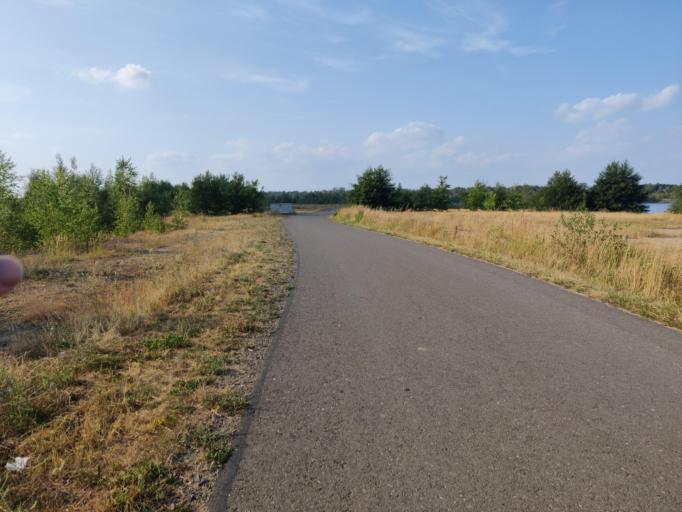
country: DE
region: Saxony
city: Neukieritzsch
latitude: 51.1728
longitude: 12.4342
